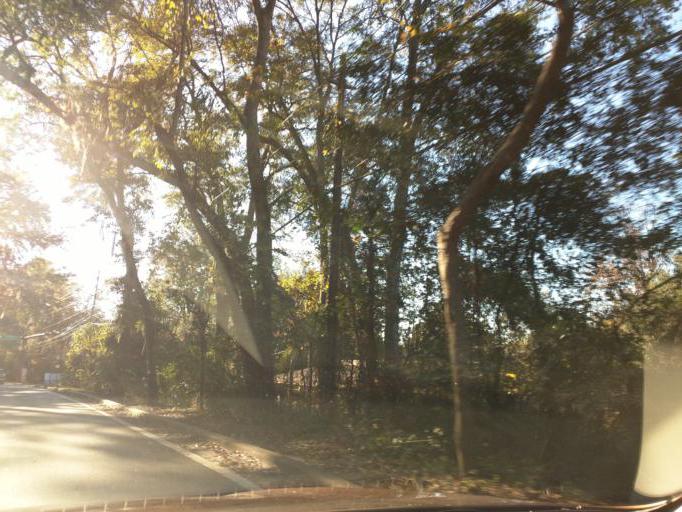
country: US
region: Florida
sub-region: Leon County
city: Tallahassee
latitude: 30.4749
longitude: -84.2227
